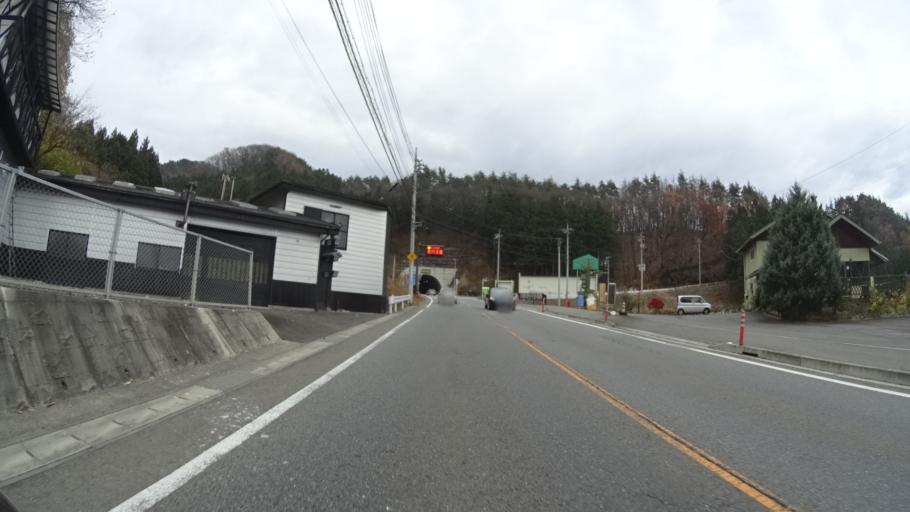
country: JP
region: Gunma
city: Numata
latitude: 36.6605
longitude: 139.1617
